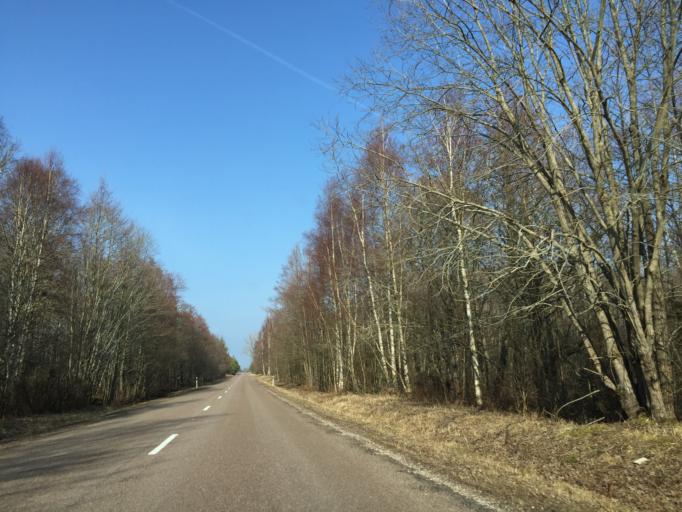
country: LV
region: Dundaga
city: Dundaga
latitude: 57.9624
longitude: 21.9977
